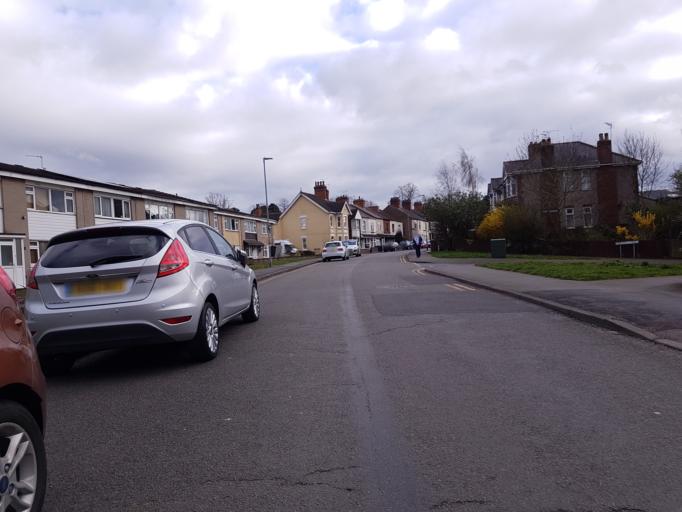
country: GB
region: England
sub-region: Leicestershire
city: Earl Shilton
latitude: 52.5728
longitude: -1.3166
